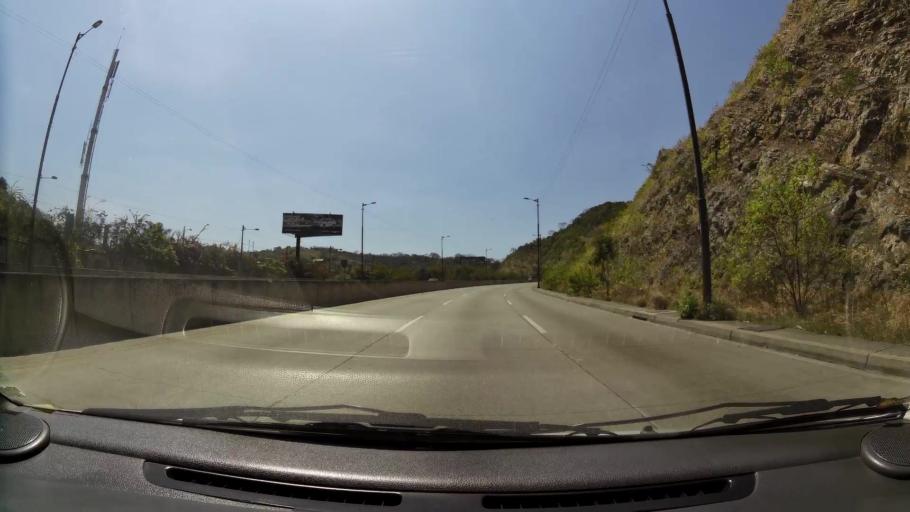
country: EC
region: Guayas
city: Guayaquil
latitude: -2.1831
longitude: -79.9309
